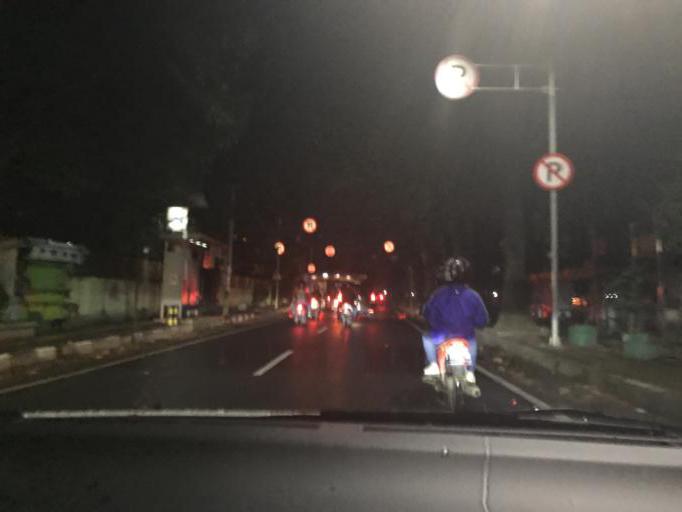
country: ID
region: West Java
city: Bandung
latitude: -6.9074
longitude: 107.6295
